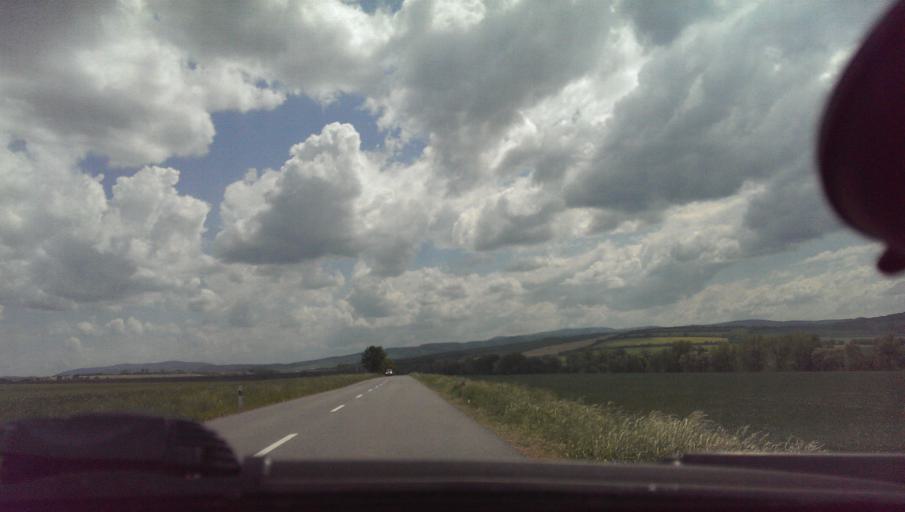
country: CZ
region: Zlin
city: Hluk
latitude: 48.9814
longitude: 17.5470
